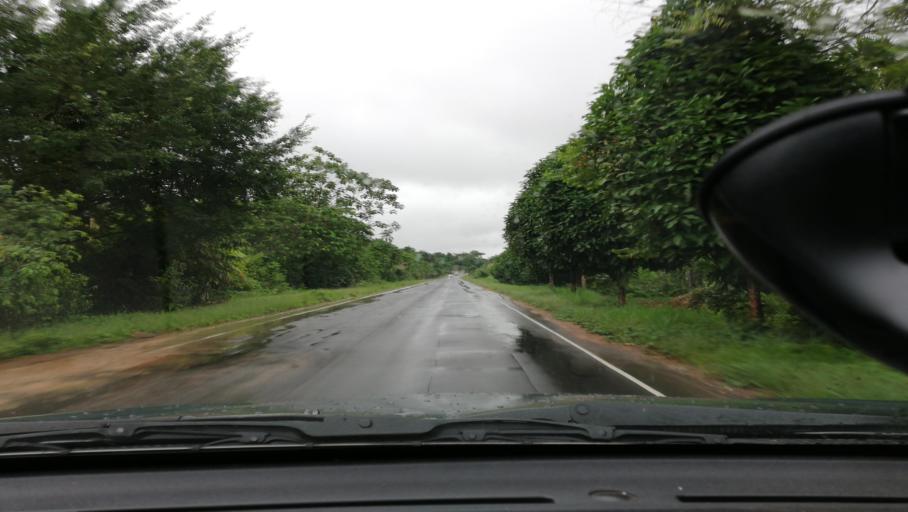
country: PE
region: Loreto
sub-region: Provincia de Maynas
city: San Juan
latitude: -4.1402
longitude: -73.4705
